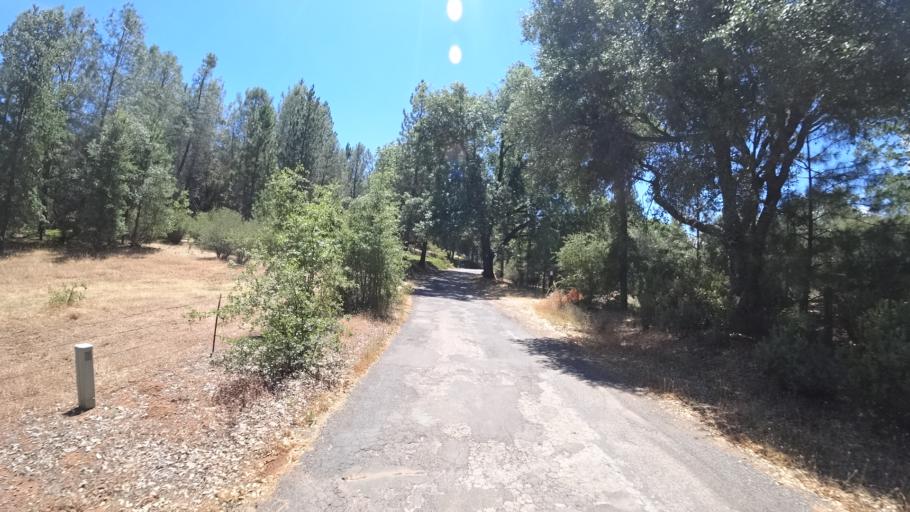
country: US
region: California
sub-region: Calaveras County
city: Forest Meadows
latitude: 38.2420
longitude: -120.4389
